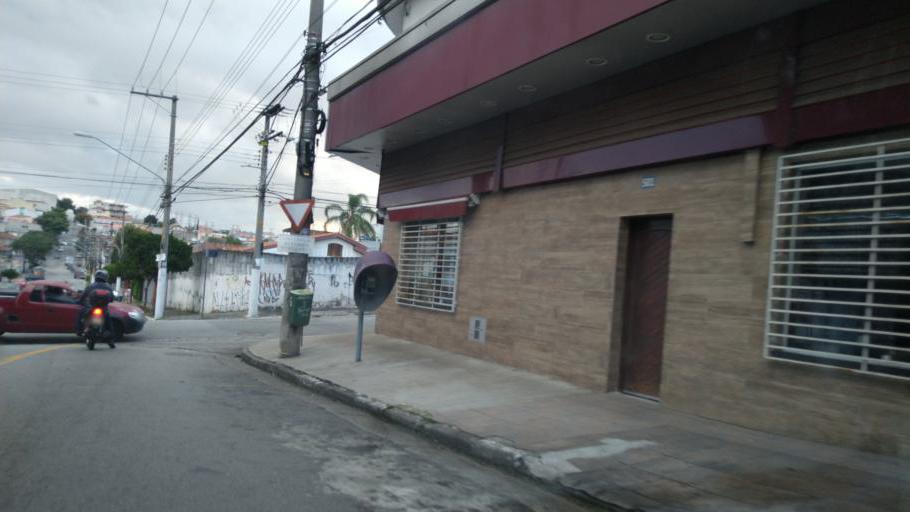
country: BR
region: Sao Paulo
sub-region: Guarulhos
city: Guarulhos
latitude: -23.4918
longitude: -46.5813
